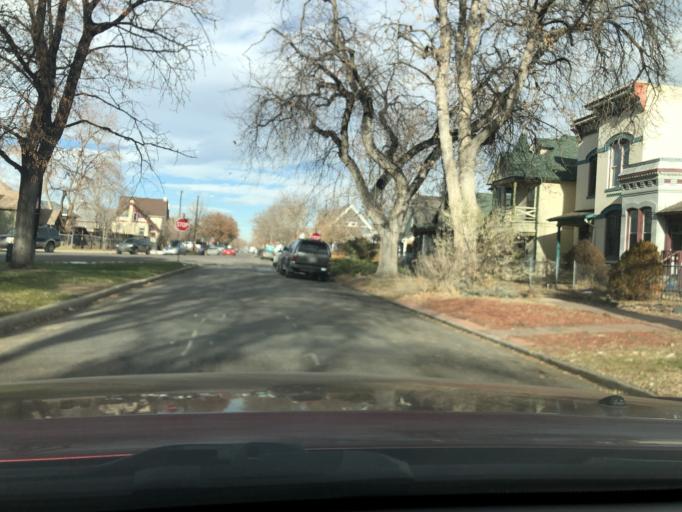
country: US
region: Colorado
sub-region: Denver County
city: Denver
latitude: 39.7559
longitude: -104.9721
